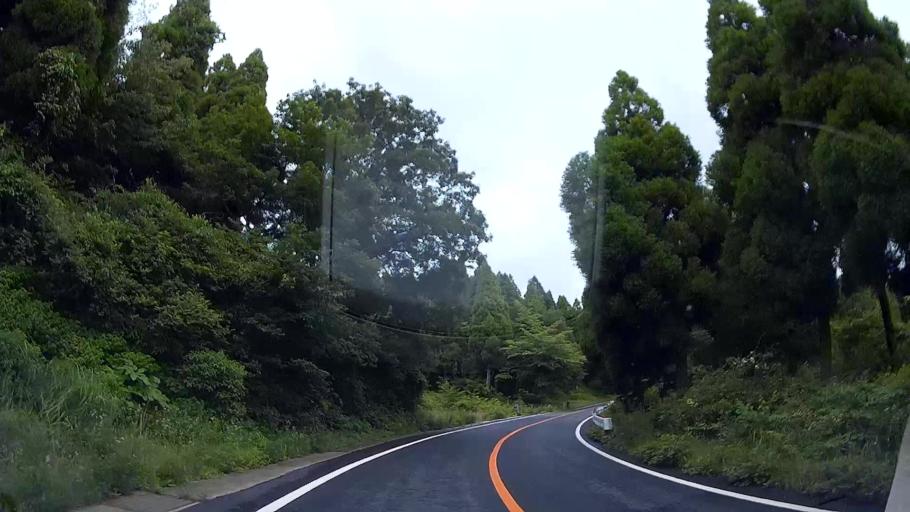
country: JP
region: Kumamoto
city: Aso
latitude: 32.8950
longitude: 131.0492
